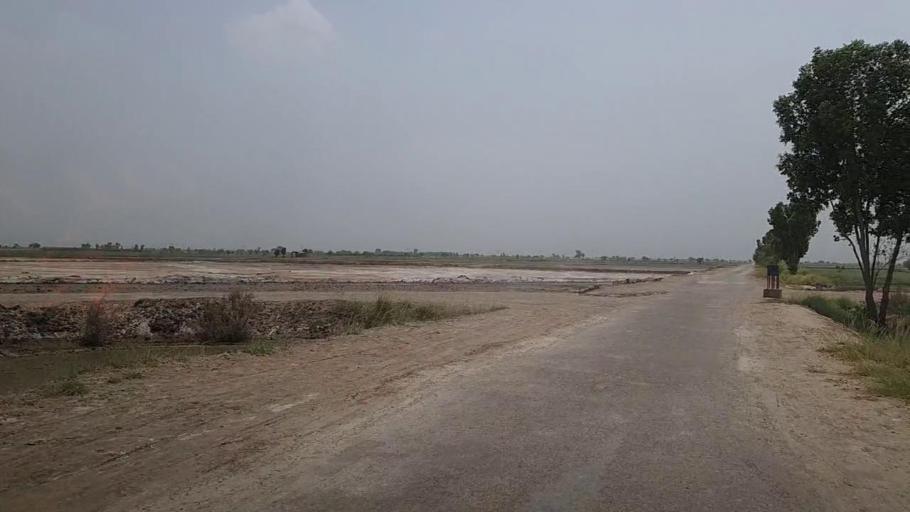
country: PK
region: Sindh
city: Sita Road
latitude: 27.0664
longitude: 67.8610
